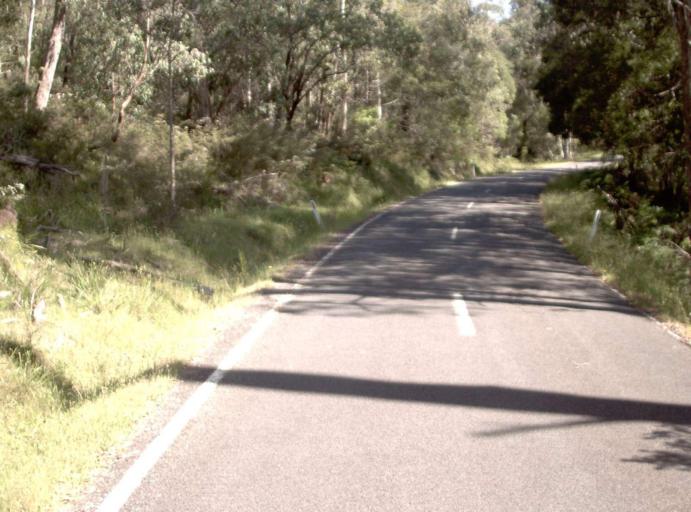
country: AU
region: New South Wales
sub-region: Bombala
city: Bombala
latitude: -37.3634
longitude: 148.6840
